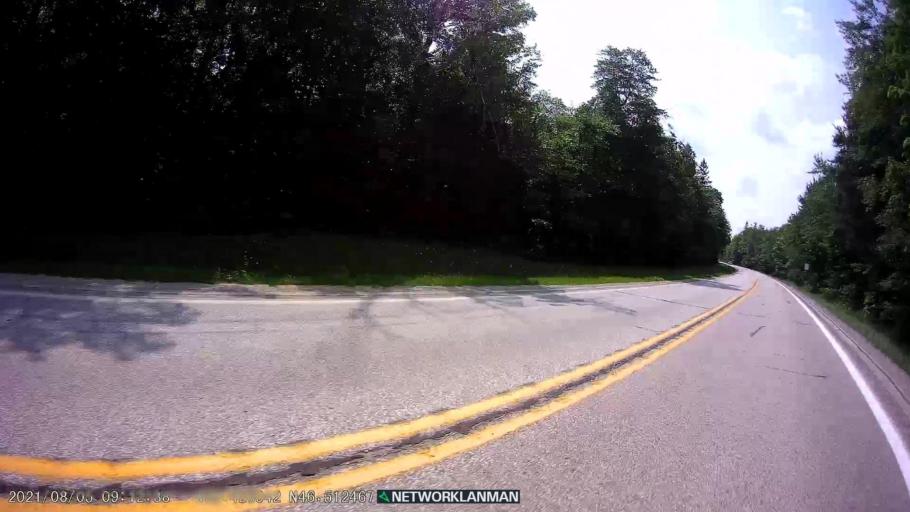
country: US
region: Michigan
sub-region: Luce County
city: Newberry
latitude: 46.5120
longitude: -85.4261
